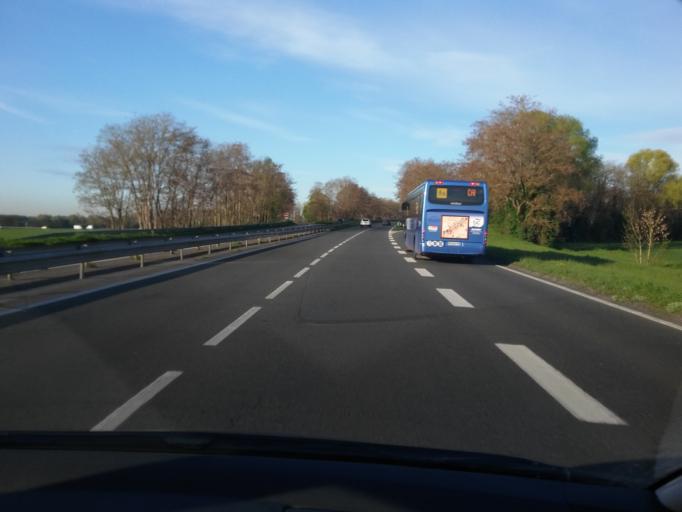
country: FR
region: Picardie
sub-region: Departement de l'Oise
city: Lacroix-Saint-Ouen
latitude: 49.3641
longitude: 2.7729
